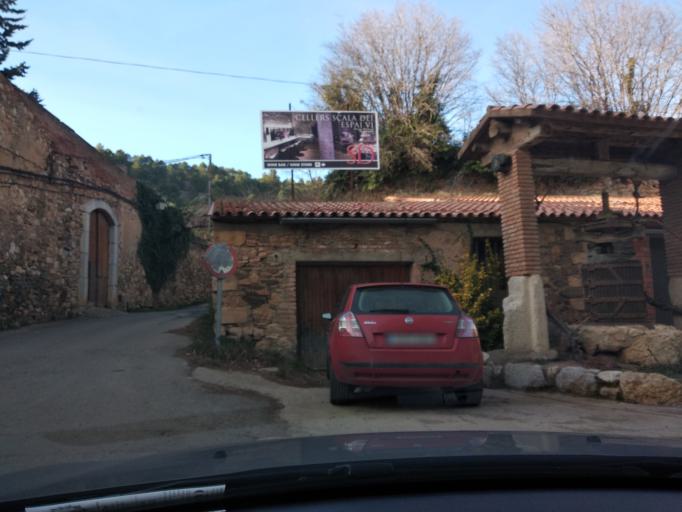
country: ES
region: Catalonia
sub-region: Provincia de Tarragona
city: la Morera de Montsant
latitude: 41.2483
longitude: 0.8117
